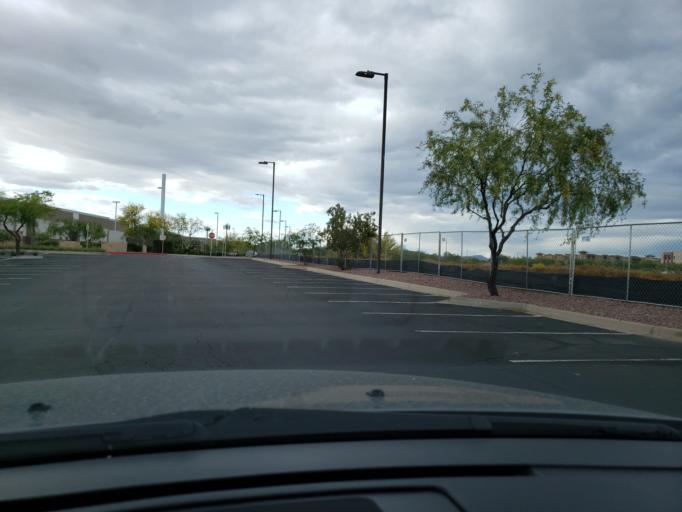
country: US
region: Arizona
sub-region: Maricopa County
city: Paradise Valley
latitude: 33.6744
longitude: -111.9701
